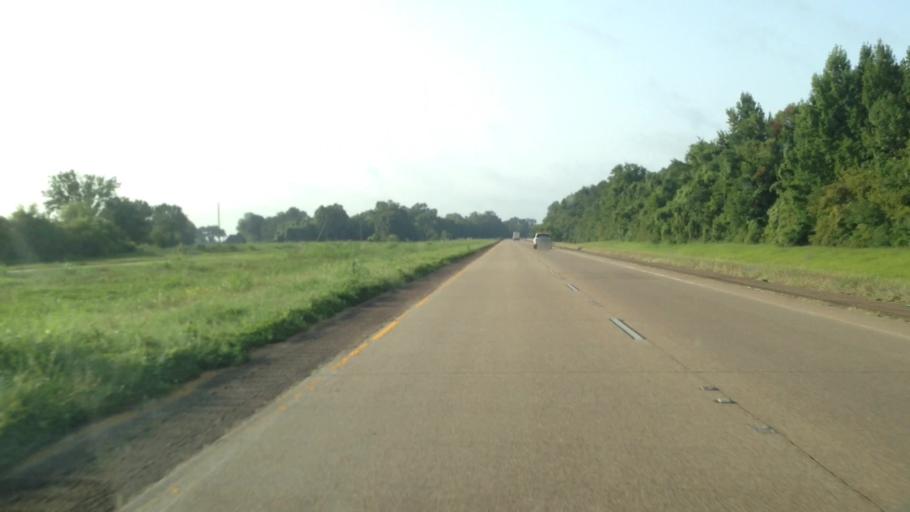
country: US
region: Louisiana
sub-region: Rapides Parish
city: Woodworth
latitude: 31.1370
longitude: -92.4492
